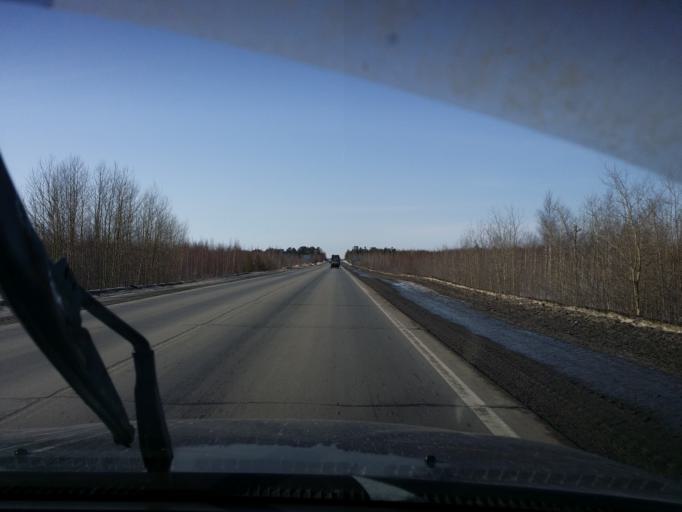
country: RU
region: Khanty-Mansiyskiy Avtonomnyy Okrug
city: Langepas
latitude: 61.1781
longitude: 75.4912
